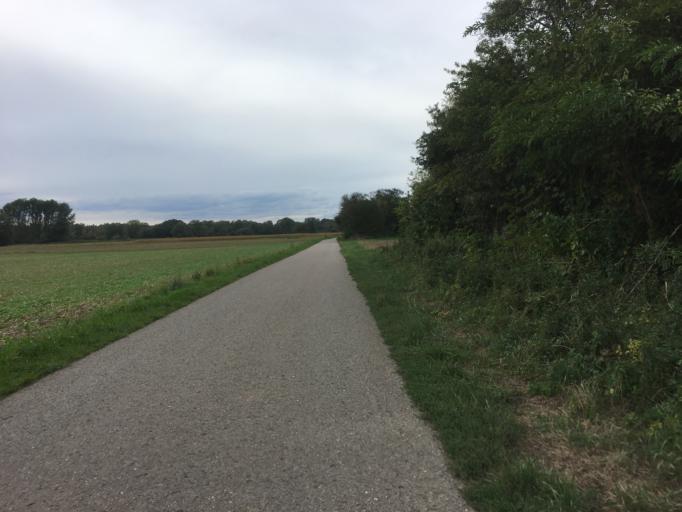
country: DE
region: Baden-Wuerttemberg
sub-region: Karlsruhe Region
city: Bruhl
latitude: 49.3983
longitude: 8.5220
